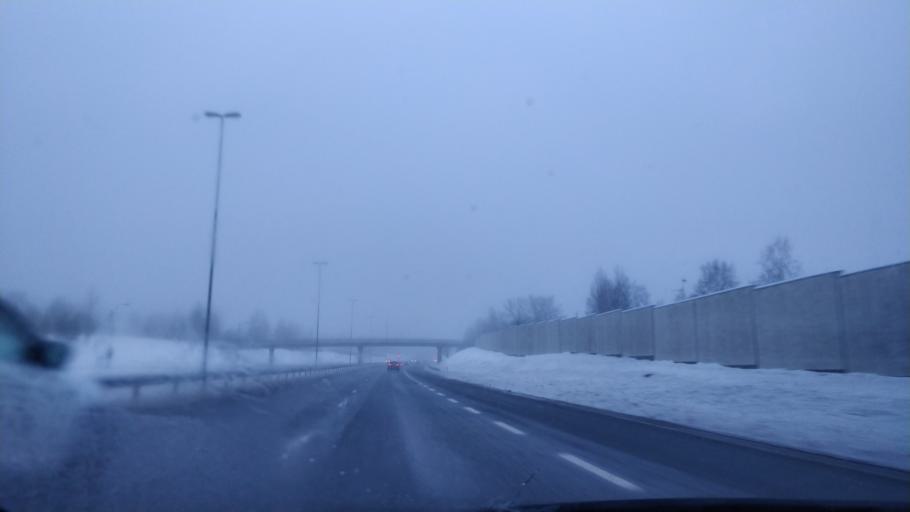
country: FI
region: Lapland
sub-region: Kemi-Tornio
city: Kemi
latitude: 65.7452
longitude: 24.5814
